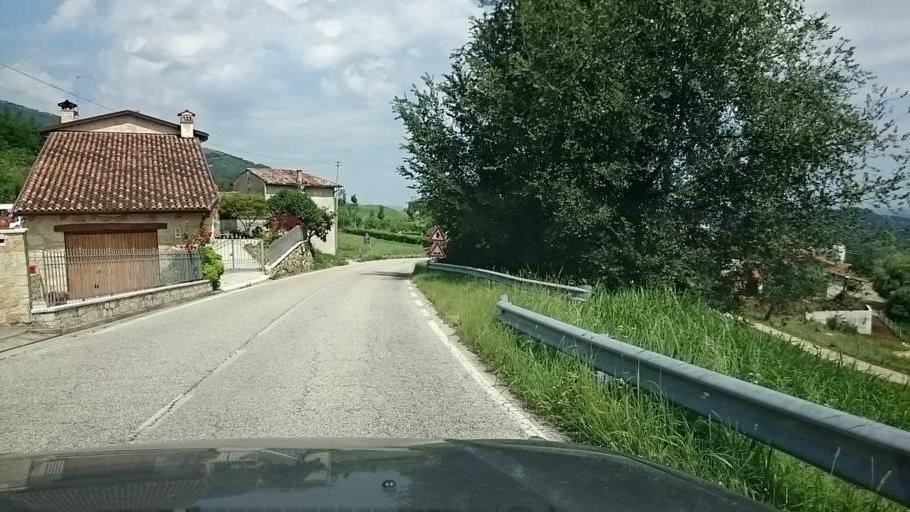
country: IT
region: Veneto
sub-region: Provincia di Vicenza
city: Pianezze
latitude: 45.7716
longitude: 11.6282
